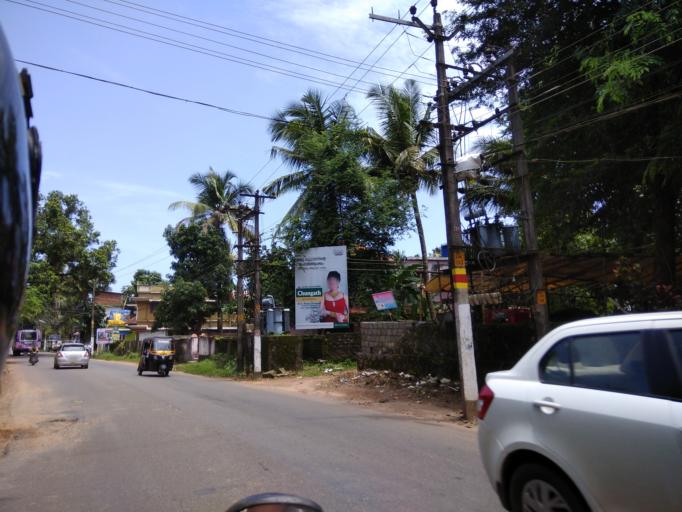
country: IN
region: Kerala
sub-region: Thrissur District
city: Trichur
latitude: 10.4972
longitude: 76.1443
